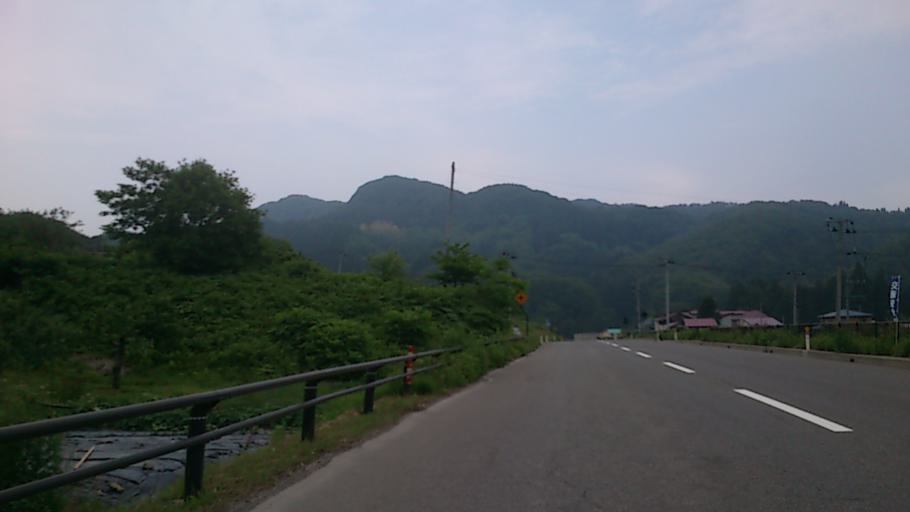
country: JP
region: Aomori
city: Hirosaki
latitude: 40.5647
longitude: 140.2896
